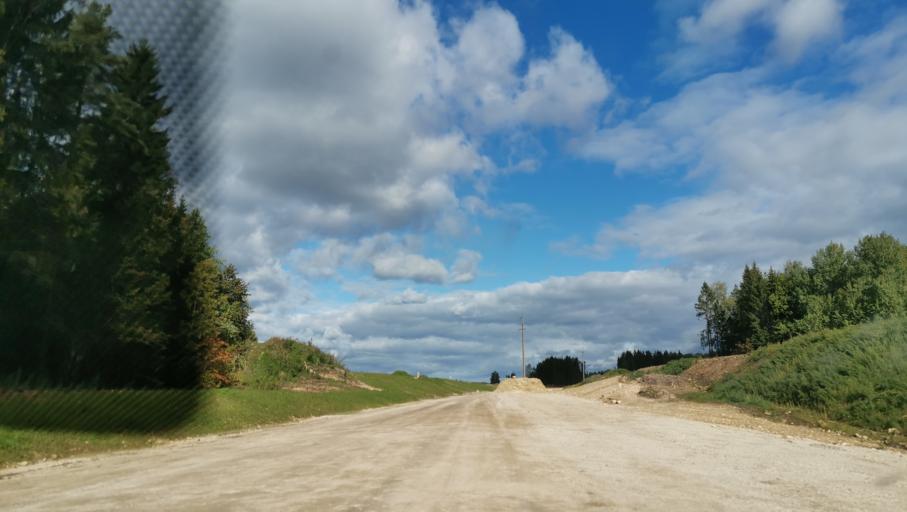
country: EE
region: Harju
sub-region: Nissi vald
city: Riisipere
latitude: 59.1316
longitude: 24.4803
